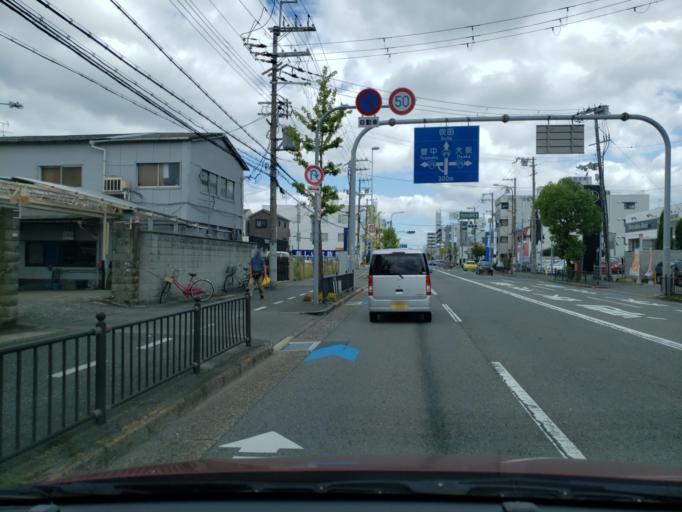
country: JP
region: Osaka
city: Toyonaka
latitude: 34.7578
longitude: 135.4697
